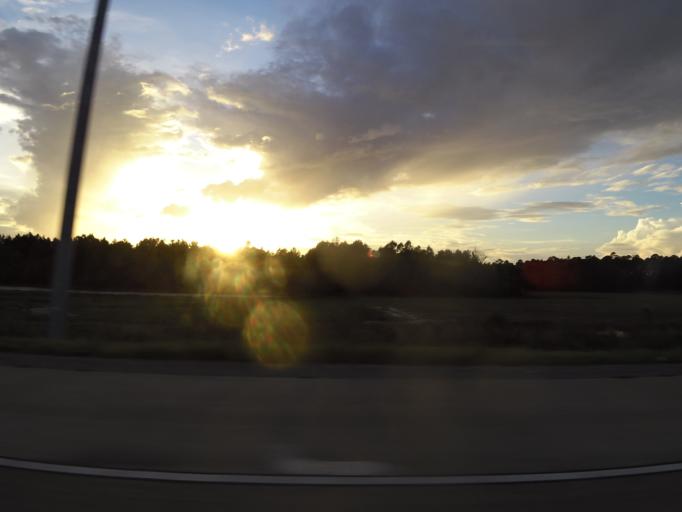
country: US
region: Georgia
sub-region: Glynn County
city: Dock Junction
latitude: 31.2409
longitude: -81.5052
